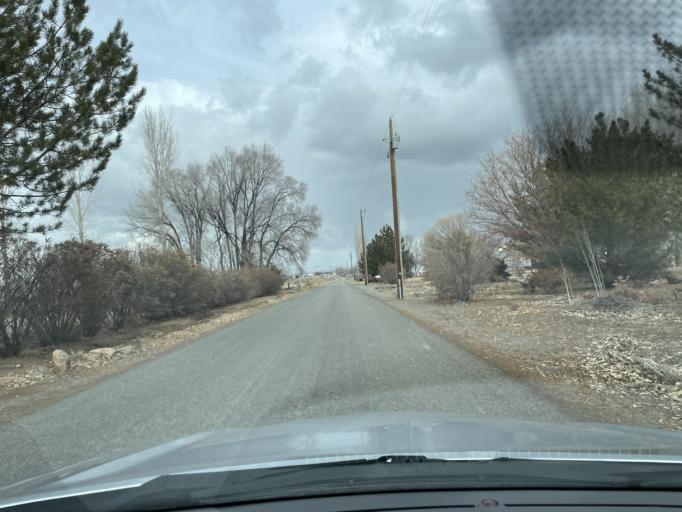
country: US
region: Colorado
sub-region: Mesa County
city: Loma
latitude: 39.1835
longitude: -108.8036
